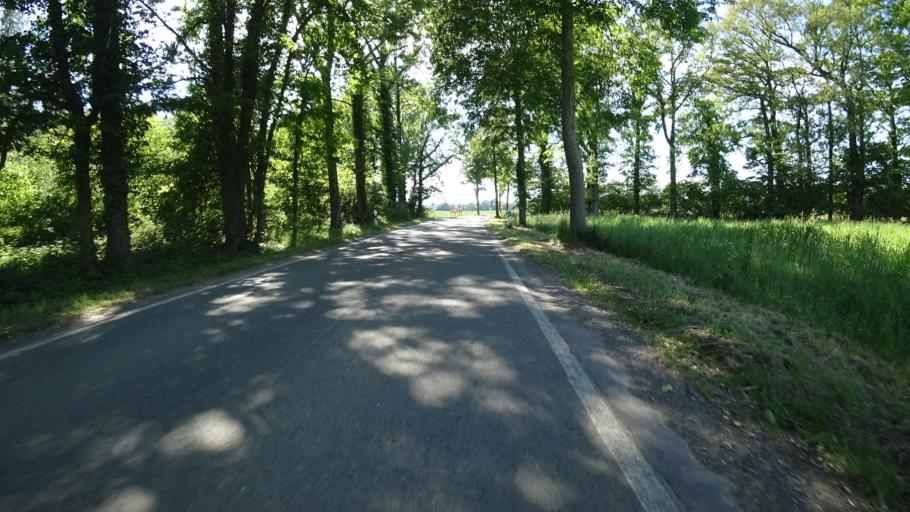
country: DE
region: North Rhine-Westphalia
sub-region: Regierungsbezirk Detmold
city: Rheda-Wiedenbruck
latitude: 51.8226
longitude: 8.2490
